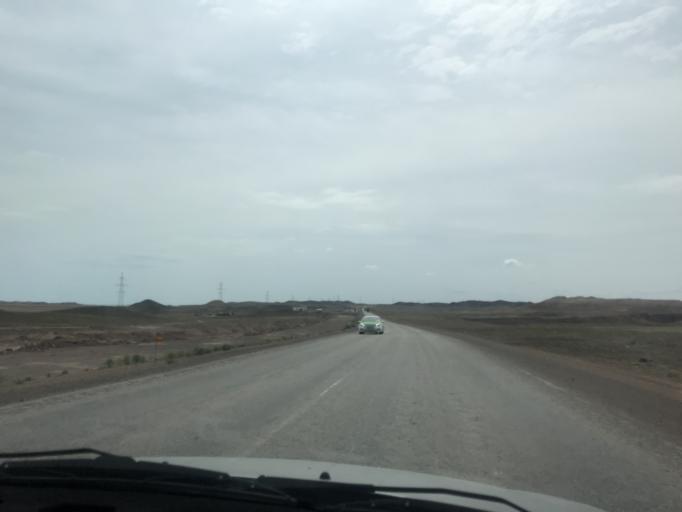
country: KZ
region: Zhambyl
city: Mynaral
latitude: 45.3679
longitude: 73.6611
